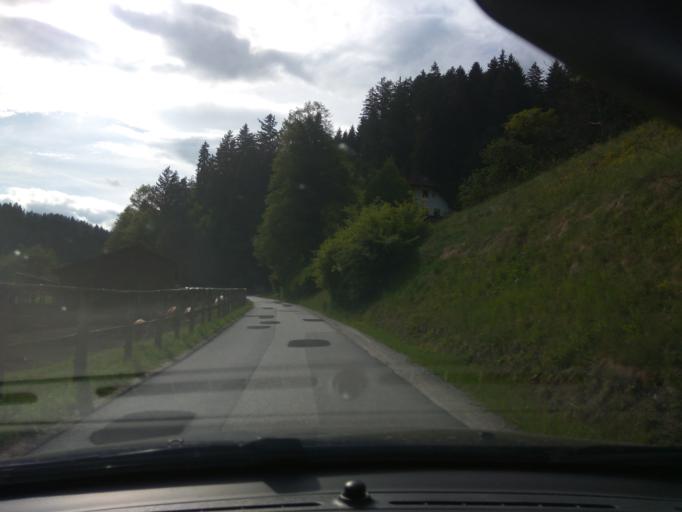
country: AT
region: Styria
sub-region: Politischer Bezirk Voitsberg
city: Voitsberg
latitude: 47.0308
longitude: 15.1188
